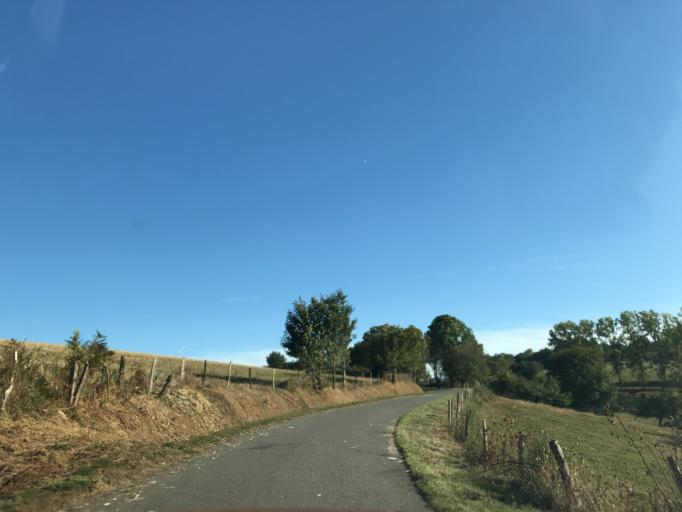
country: FR
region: Auvergne
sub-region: Departement du Puy-de-Dome
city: Escoutoux
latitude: 45.7685
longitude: 3.6262
